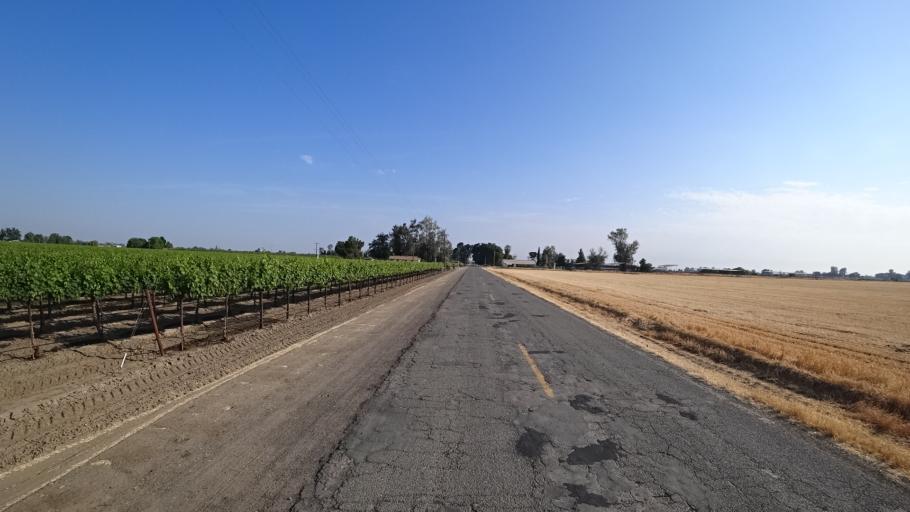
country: US
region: California
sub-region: Fresno County
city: Riverdale
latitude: 36.3697
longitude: -119.8431
